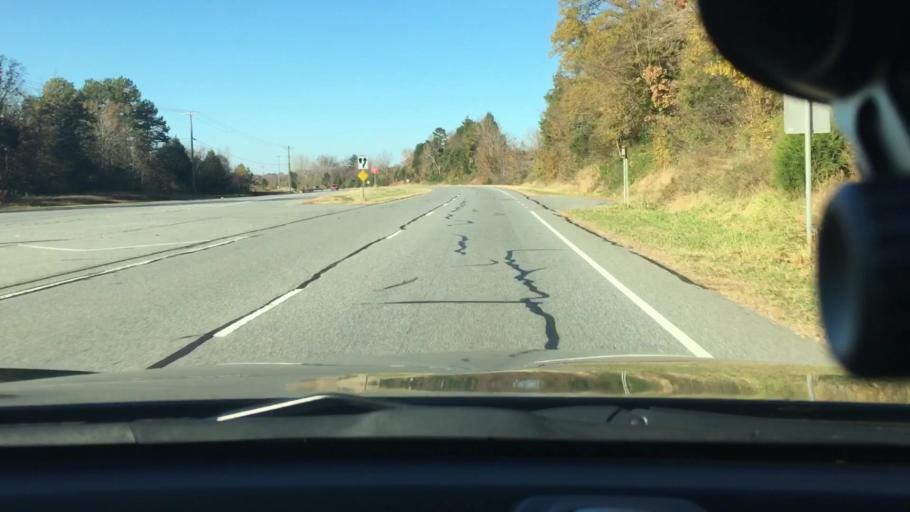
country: US
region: North Carolina
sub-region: Cabarrus County
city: Concord
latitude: 35.3854
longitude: -80.5190
